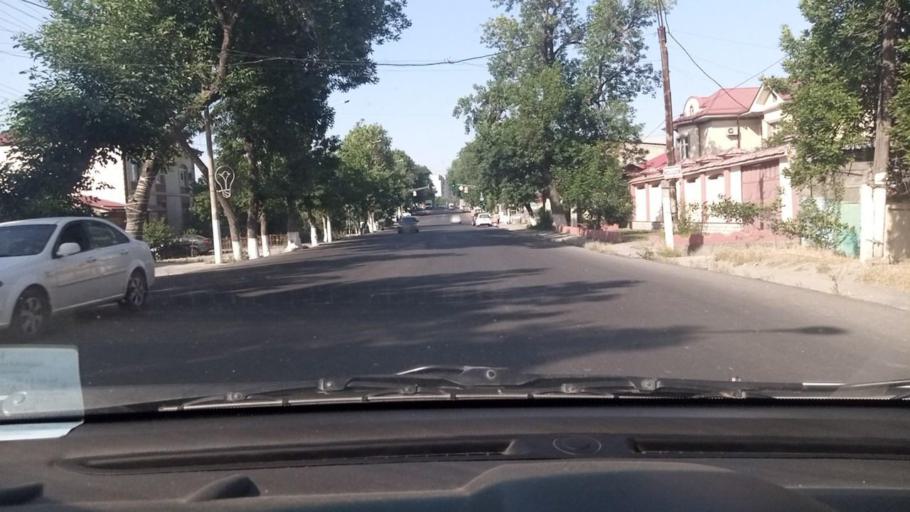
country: UZ
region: Toshkent
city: Salor
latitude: 41.3171
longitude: 69.3382
